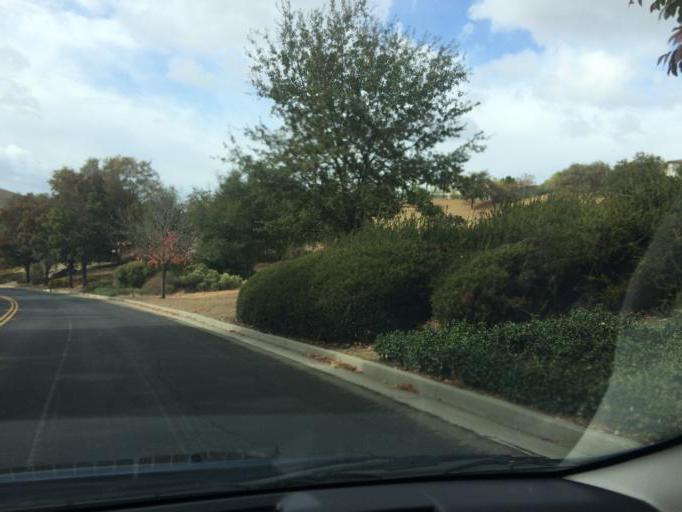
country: US
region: California
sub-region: Santa Clara County
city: Seven Trees
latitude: 37.2852
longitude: -121.7696
